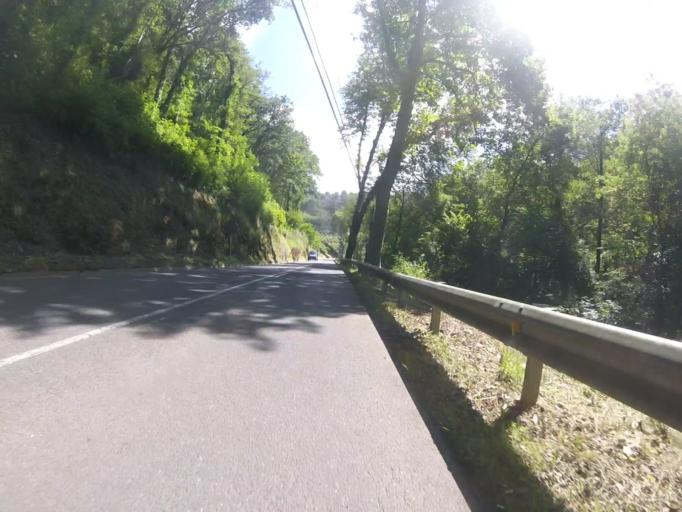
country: ES
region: Basque Country
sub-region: Provincia de Guipuzcoa
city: Azpeitia
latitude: 43.1773
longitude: -2.2502
